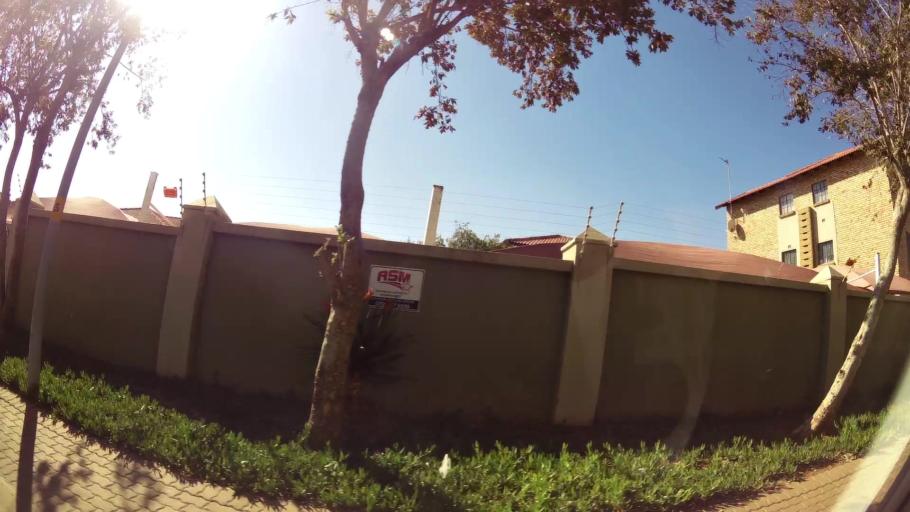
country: ZA
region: Gauteng
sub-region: Ekurhuleni Metropolitan Municipality
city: Germiston
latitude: -26.2909
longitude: 28.1021
